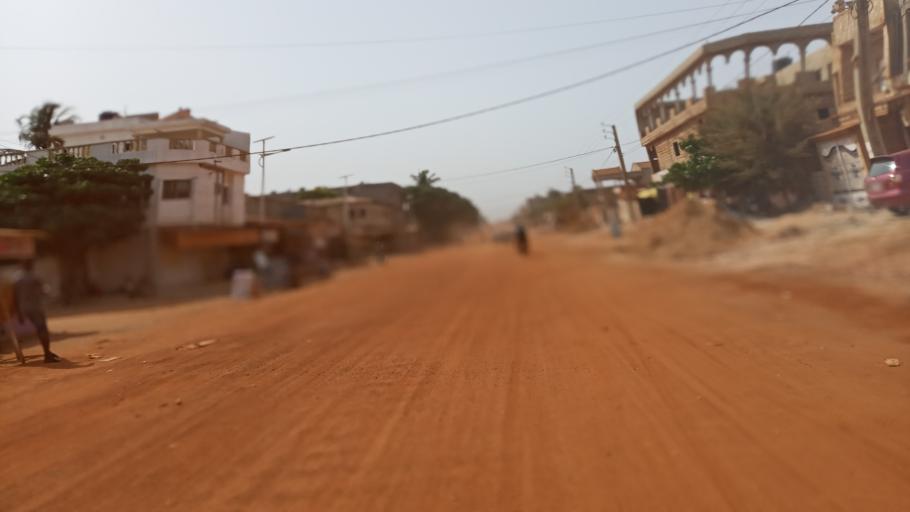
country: TG
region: Maritime
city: Lome
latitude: 6.1989
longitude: 1.1710
